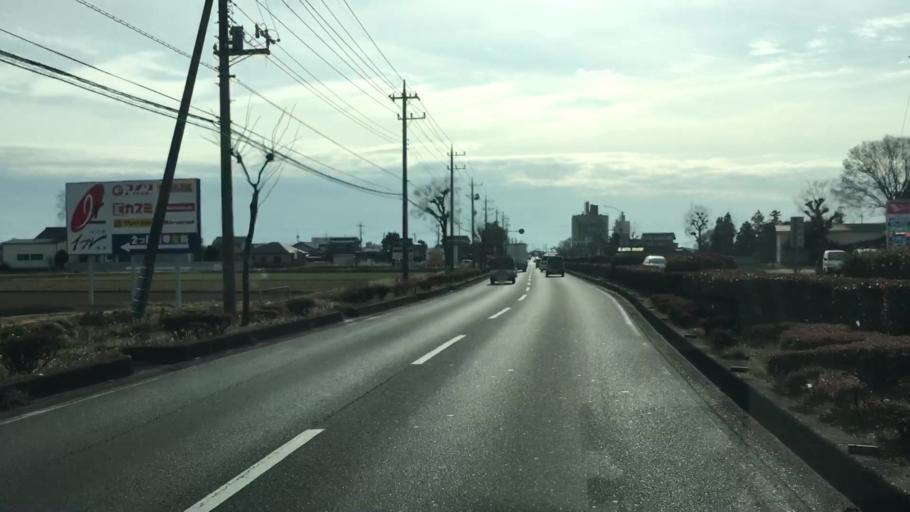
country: JP
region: Saitama
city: Menuma
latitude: 36.2133
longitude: 139.3693
